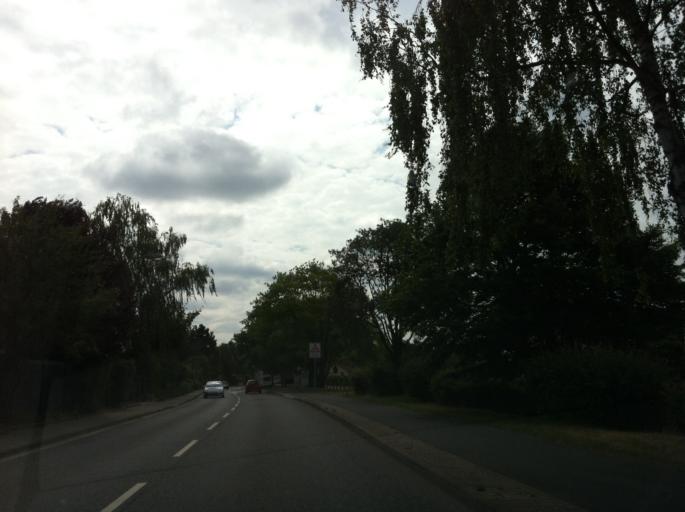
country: DE
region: Hesse
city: Sulzbach
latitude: 50.1104
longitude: 8.5247
